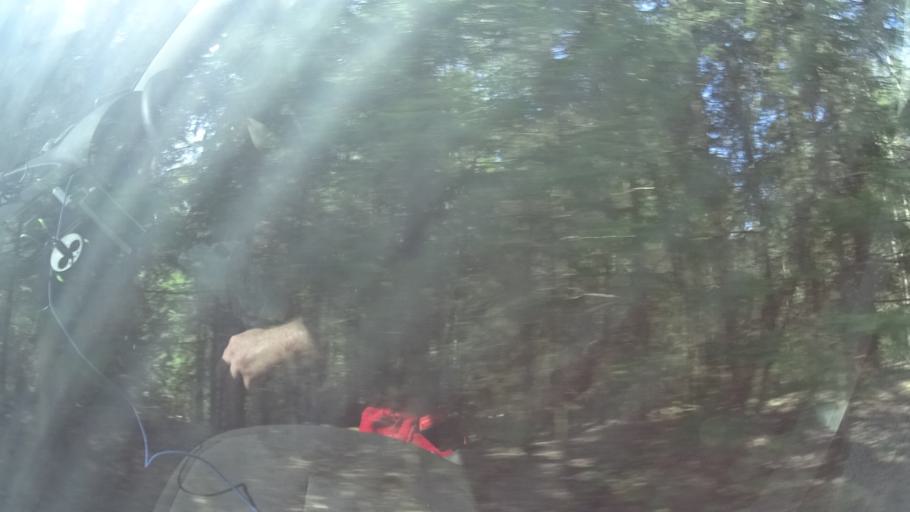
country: DE
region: Thuringia
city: Hildburghausen
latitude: 50.4571
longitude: 10.7784
